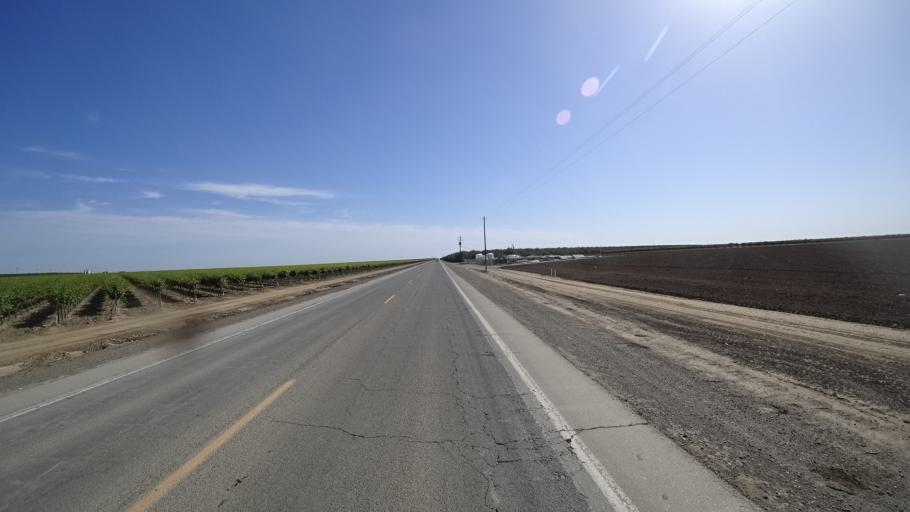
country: US
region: California
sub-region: Fresno County
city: Huron
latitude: 36.1512
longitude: -119.9942
